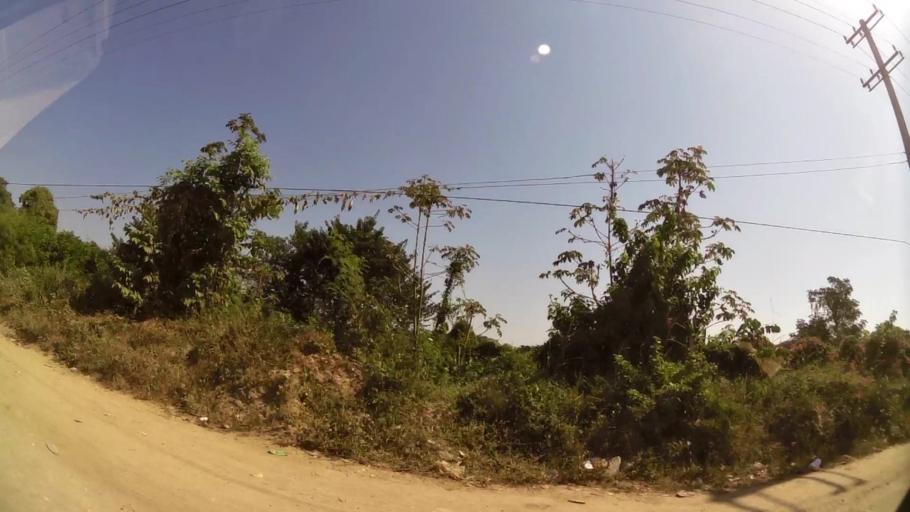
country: CO
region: Bolivar
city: Cartagena
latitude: 10.3644
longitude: -75.4904
